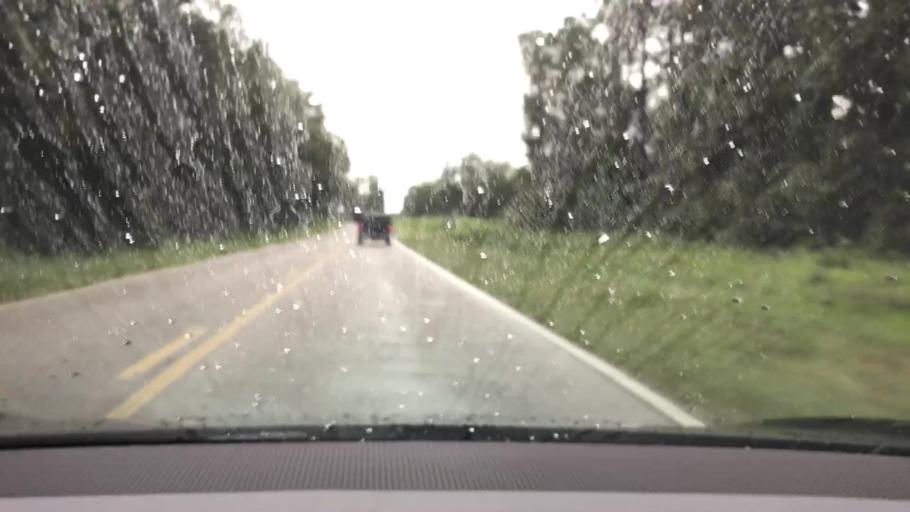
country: US
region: Alabama
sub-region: Geneva County
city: Samson
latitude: 31.1359
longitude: -86.1354
